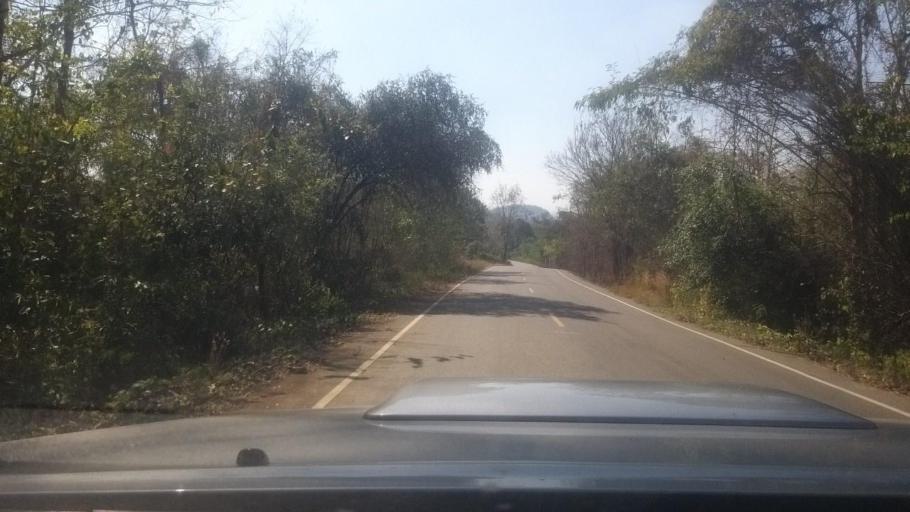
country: TH
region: Phrae
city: Nong Muang Khai
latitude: 18.2960
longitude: 100.0417
